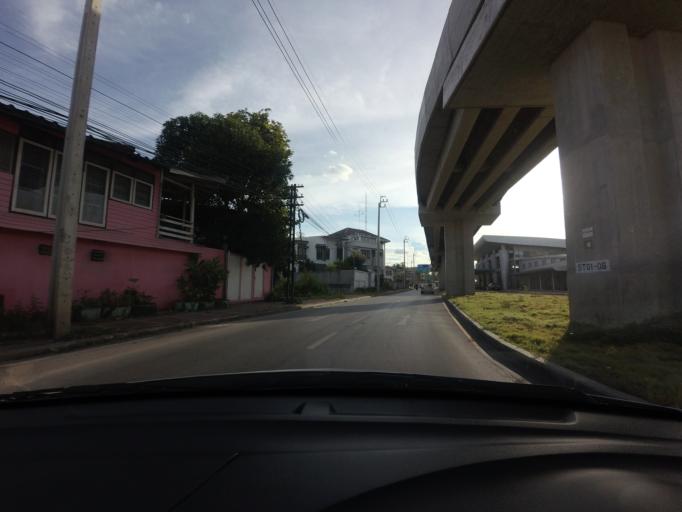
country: TH
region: Nonthaburi
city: Bang Kruai
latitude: 13.7918
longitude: 100.4787
